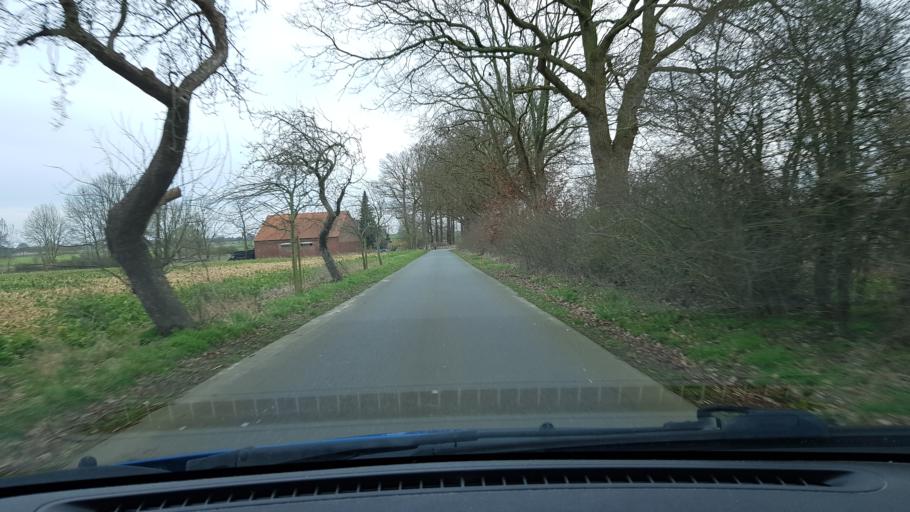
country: DE
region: Lower Saxony
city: Oetzen
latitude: 53.0071
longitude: 10.6533
